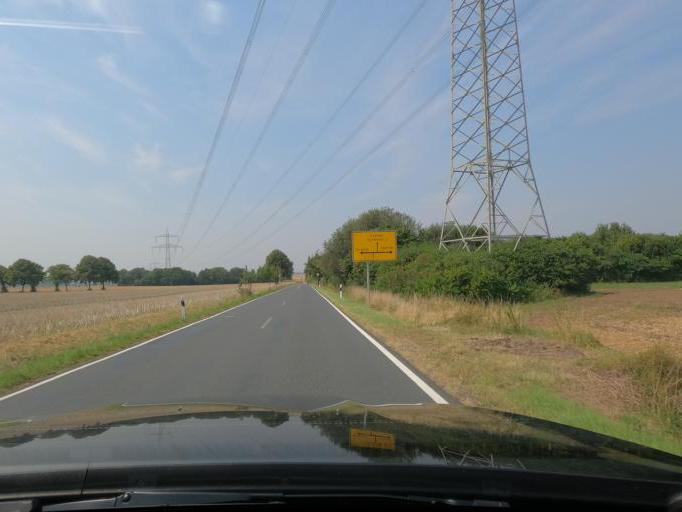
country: DE
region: Lower Saxony
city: Algermissen
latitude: 52.2741
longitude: 9.9074
